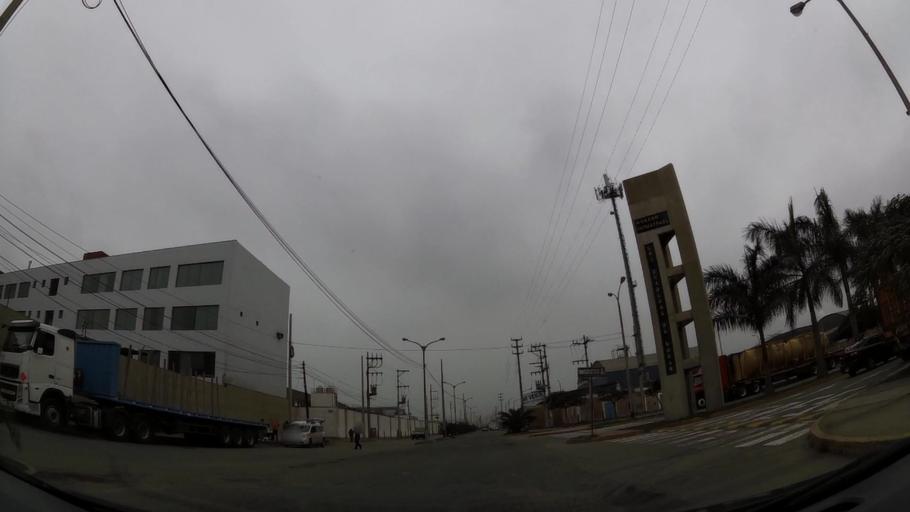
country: PE
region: Lima
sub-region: Lima
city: Punta Hermosa
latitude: -12.2952
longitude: -76.8380
